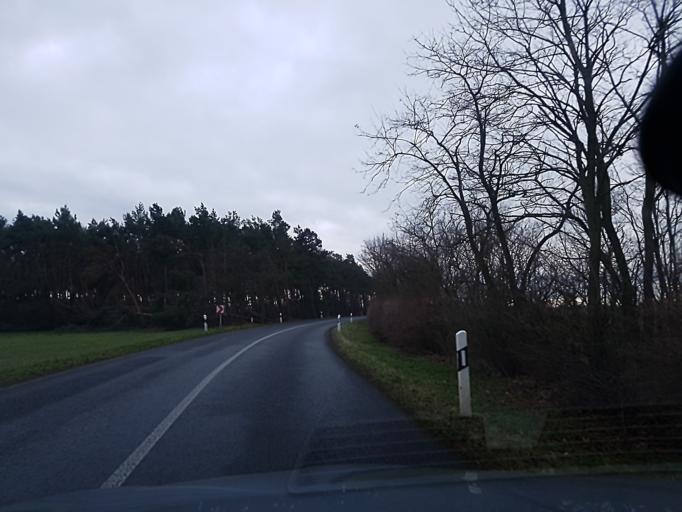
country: DE
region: Brandenburg
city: Bad Liebenwerda
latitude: 51.5412
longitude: 13.3147
